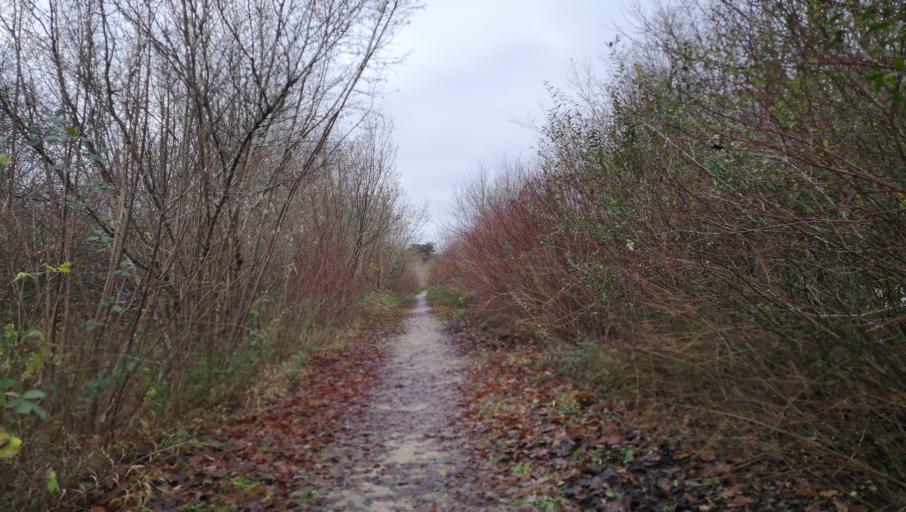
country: FR
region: Centre
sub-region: Departement du Loiret
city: Saint-Jean-de-Braye
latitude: 47.9106
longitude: 1.9880
